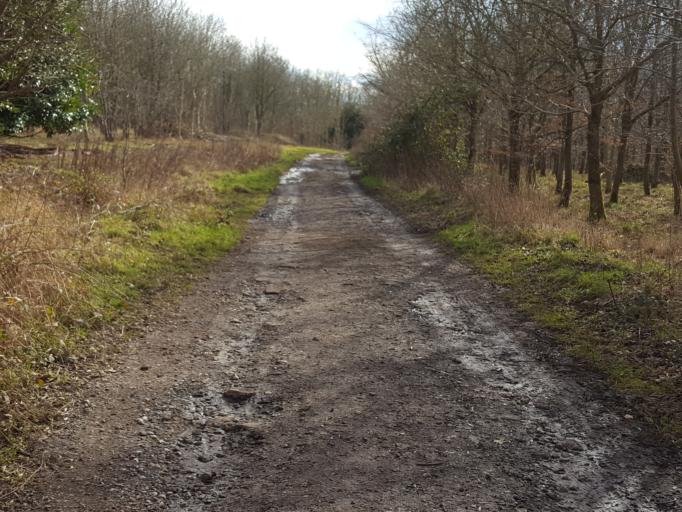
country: GB
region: England
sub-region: Buckinghamshire
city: High Wycombe
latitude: 51.6535
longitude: -0.8110
